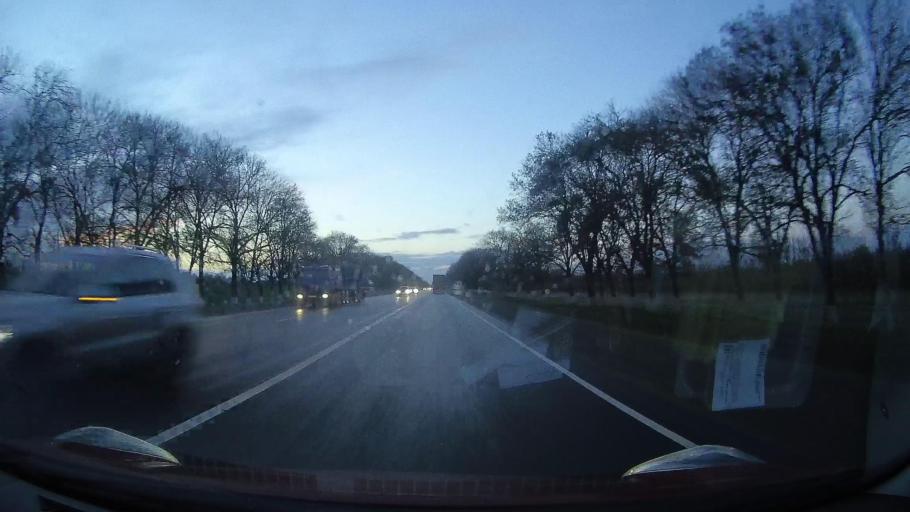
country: RU
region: Krasnodarskiy
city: Konokovo
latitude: 44.8381
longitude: 41.3211
